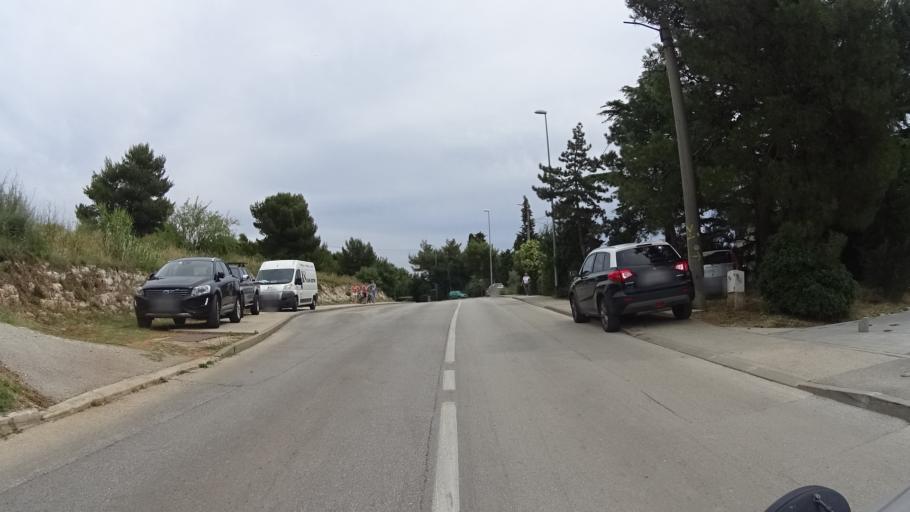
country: HR
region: Istarska
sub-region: Grad Pula
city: Pula
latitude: 44.8615
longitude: 13.8199
